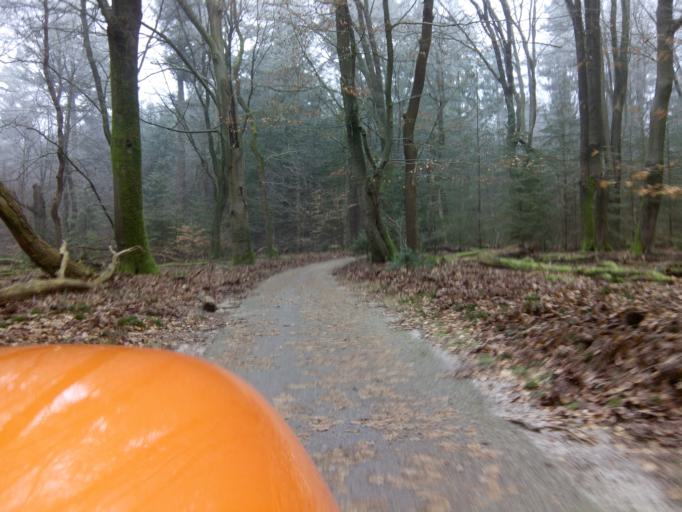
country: NL
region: Gelderland
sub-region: Gemeente Barneveld
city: Garderen
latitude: 52.2588
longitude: 5.6857
